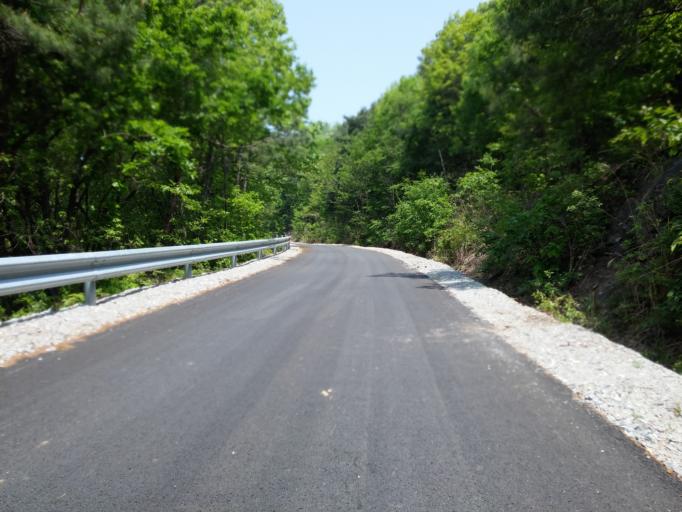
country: KR
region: Chungcheongbuk-do
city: Okcheon
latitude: 36.4221
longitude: 127.5832
